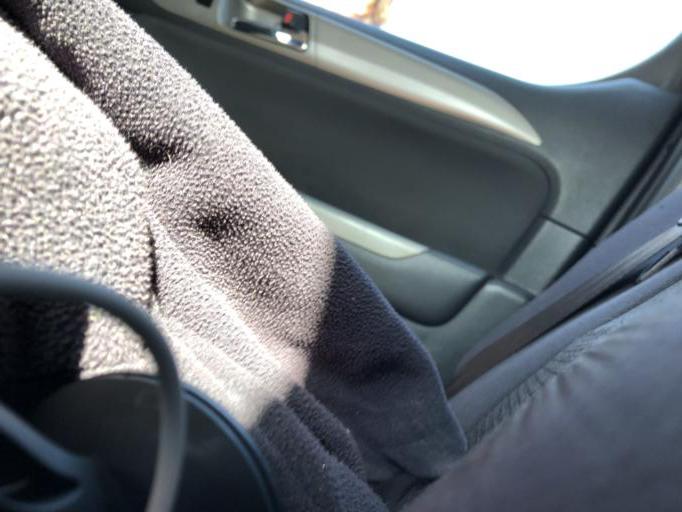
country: CL
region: Santiago Metropolitan
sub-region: Provincia de Cordillera
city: Puente Alto
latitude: -33.5683
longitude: -70.5734
